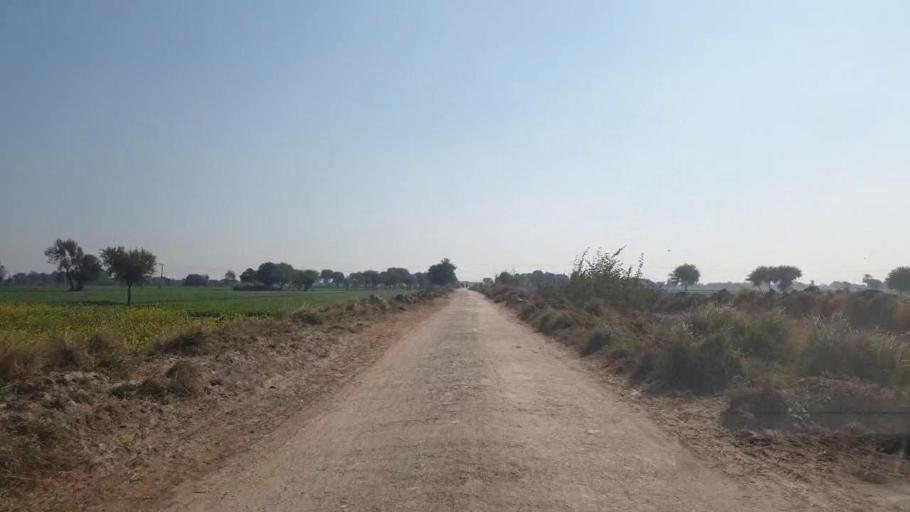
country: PK
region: Sindh
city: Shahdadpur
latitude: 25.9591
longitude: 68.6243
